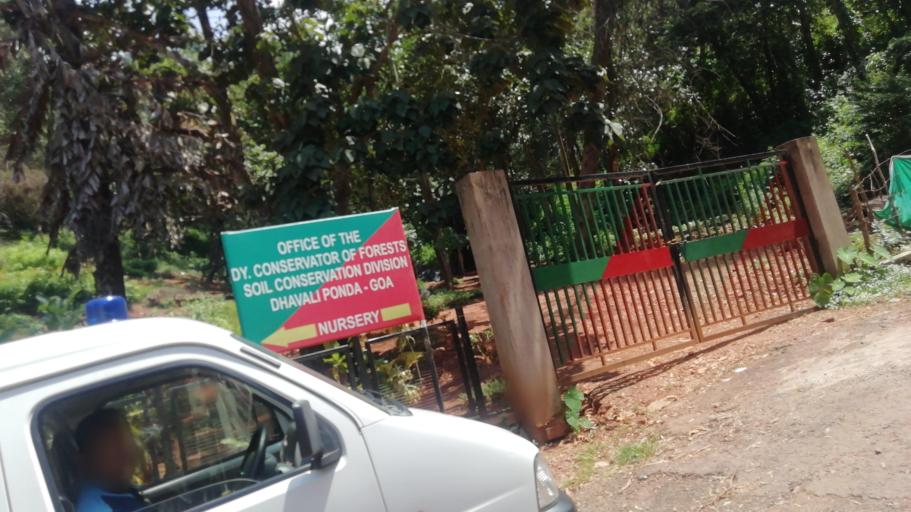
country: IN
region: Goa
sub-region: North Goa
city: Ponda
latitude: 15.3879
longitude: 74.0064
